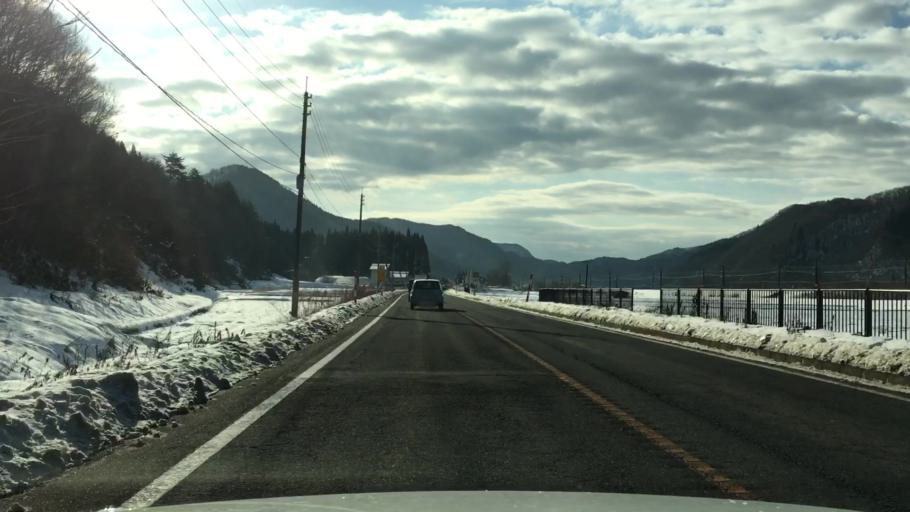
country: JP
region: Akita
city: Odate
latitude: 40.3613
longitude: 140.5968
